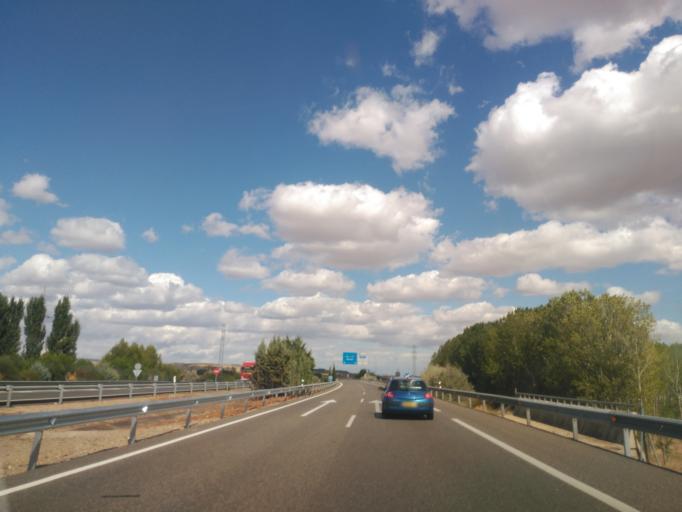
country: ES
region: Castille and Leon
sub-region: Provincia de Palencia
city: Soto de Cerrato
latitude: 41.9776
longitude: -4.4409
